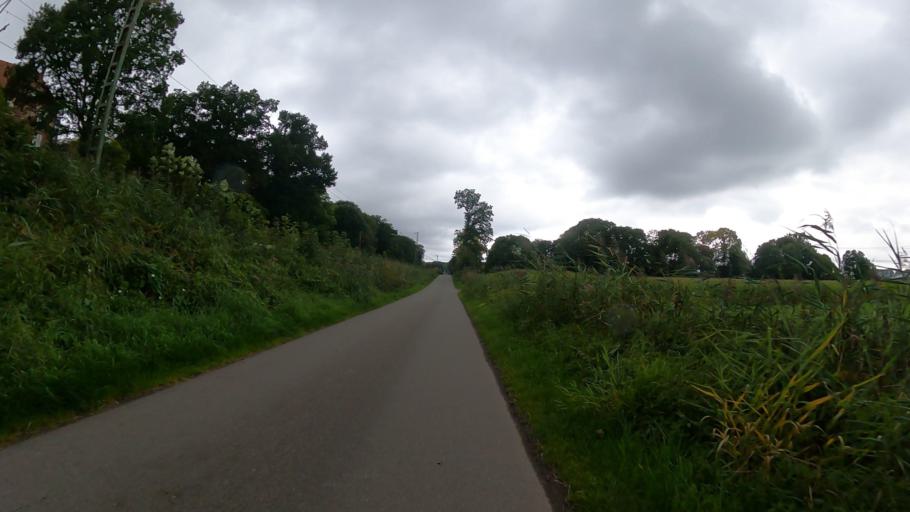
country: DE
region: Lower Saxony
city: Agathenburg
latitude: 53.5620
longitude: 9.5362
